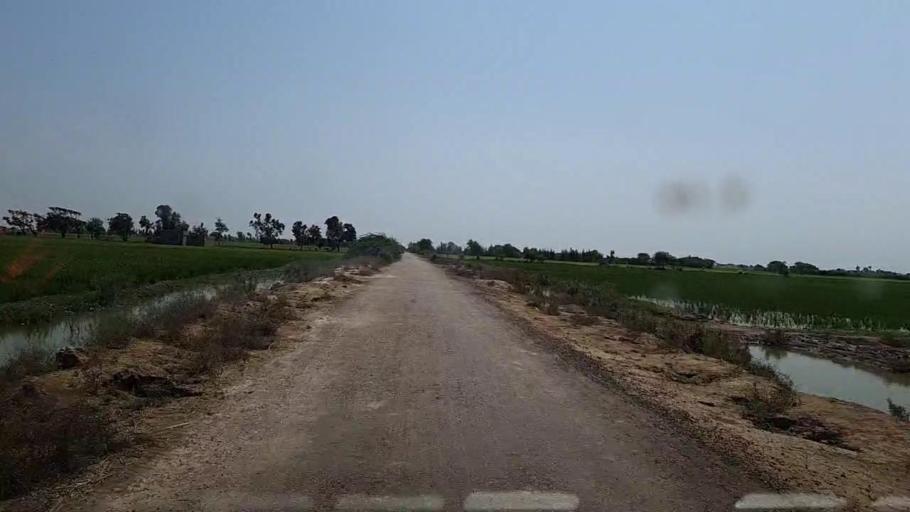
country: PK
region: Sindh
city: Mirpur Batoro
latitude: 24.6186
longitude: 68.4522
